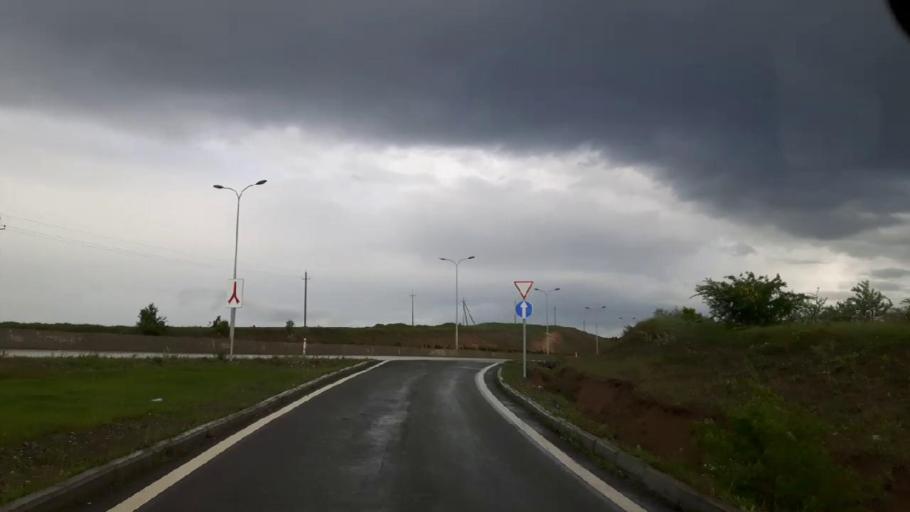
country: GE
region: Shida Kartli
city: Gori
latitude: 42.0134
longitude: 44.0344
